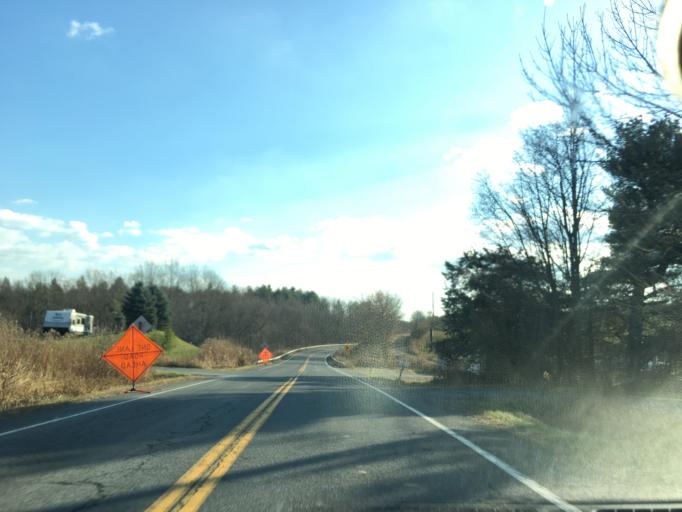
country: US
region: New York
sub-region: Rensselaer County
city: West Sand Lake
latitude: 42.6086
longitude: -73.6191
